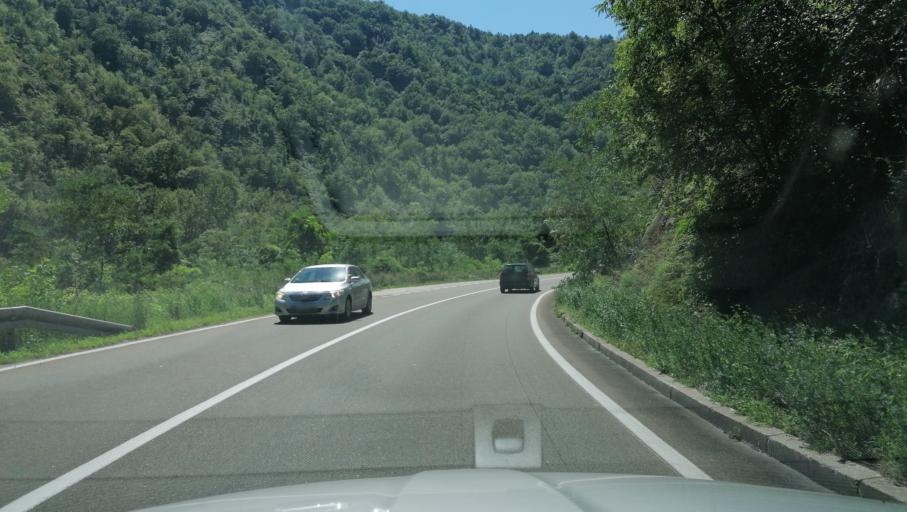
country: RS
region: Central Serbia
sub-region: Raski Okrug
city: Kraljevo
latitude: 43.5589
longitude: 20.6195
